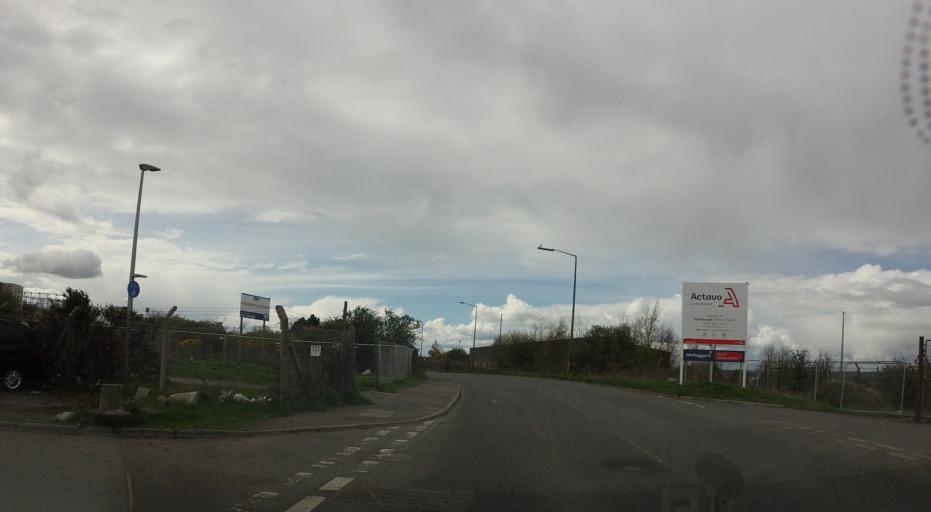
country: GB
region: Scotland
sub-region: Edinburgh
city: Edinburgh
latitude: 55.9832
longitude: -3.2339
